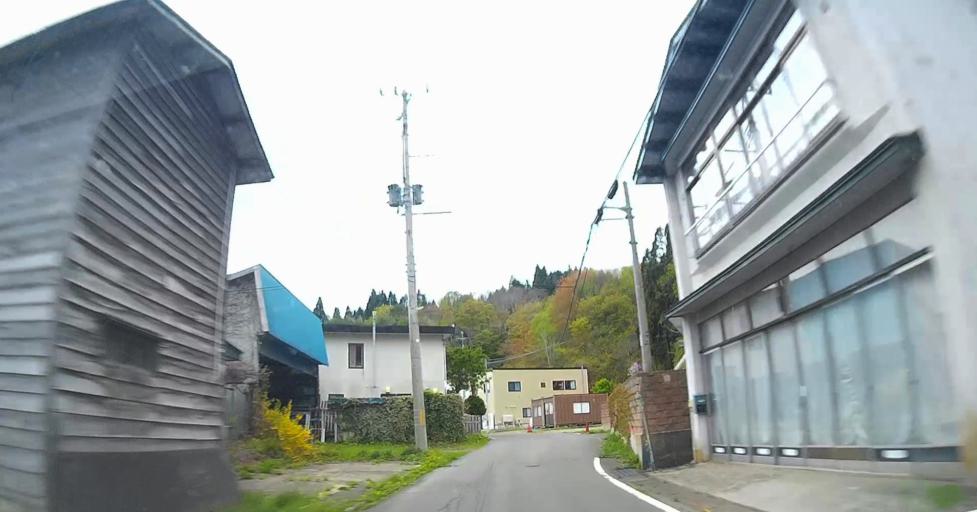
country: JP
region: Aomori
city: Shimokizukuri
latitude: 41.1976
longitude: 140.4300
